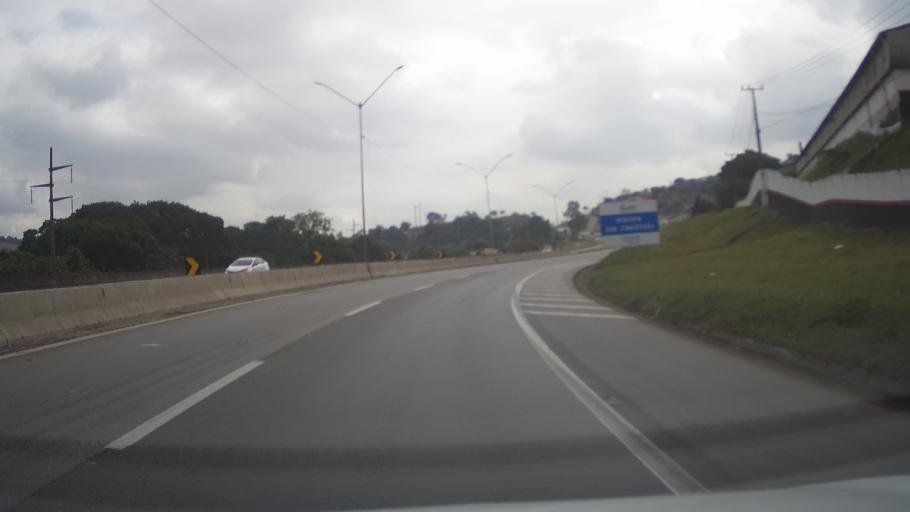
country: BR
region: Minas Gerais
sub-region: Extrema
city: Extrema
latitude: -22.8260
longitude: -46.3132
